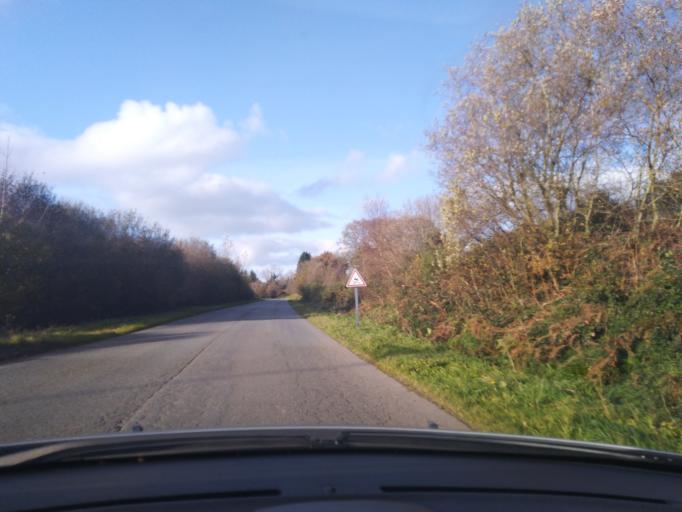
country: FR
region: Brittany
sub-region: Departement du Finistere
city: Guerlesquin
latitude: 48.5200
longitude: -3.5859
